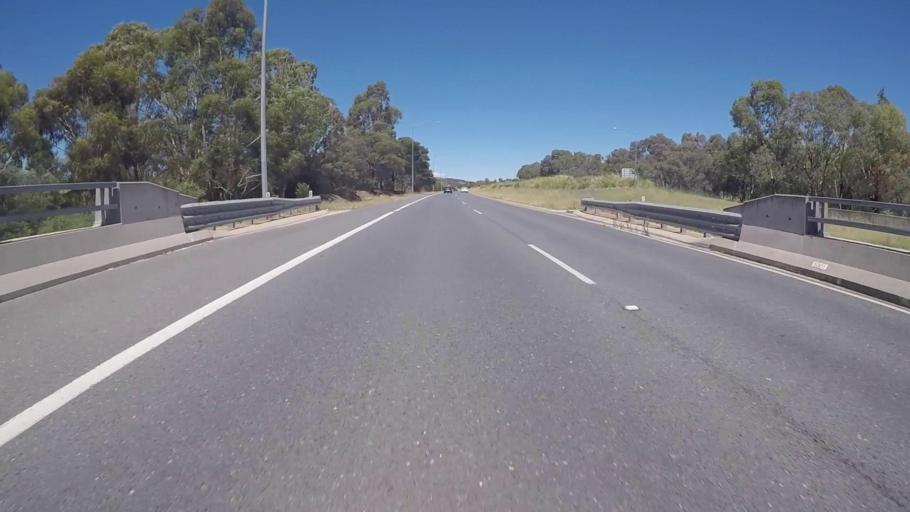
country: AU
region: Australian Capital Territory
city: Macarthur
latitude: -35.4172
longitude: 149.0755
